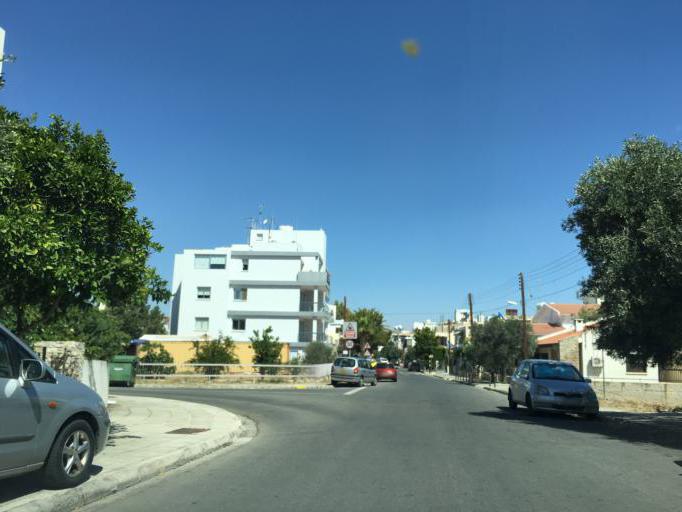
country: CY
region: Lefkosia
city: Nicosia
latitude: 35.1554
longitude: 33.3151
